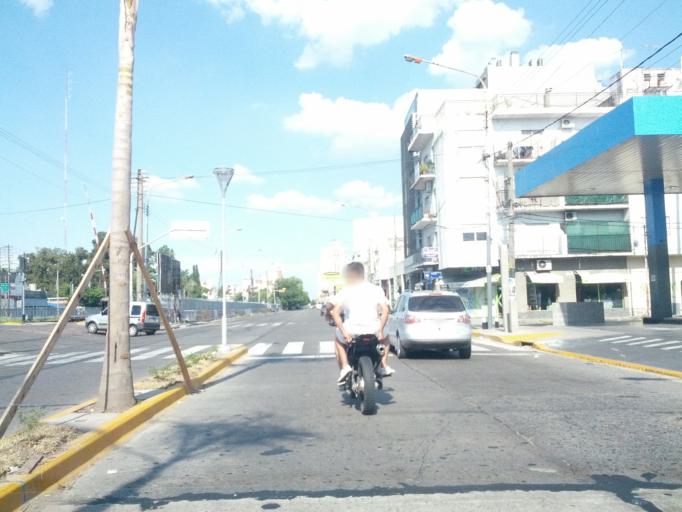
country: AR
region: Buenos Aires
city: San Justo
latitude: -34.6428
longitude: -58.5780
